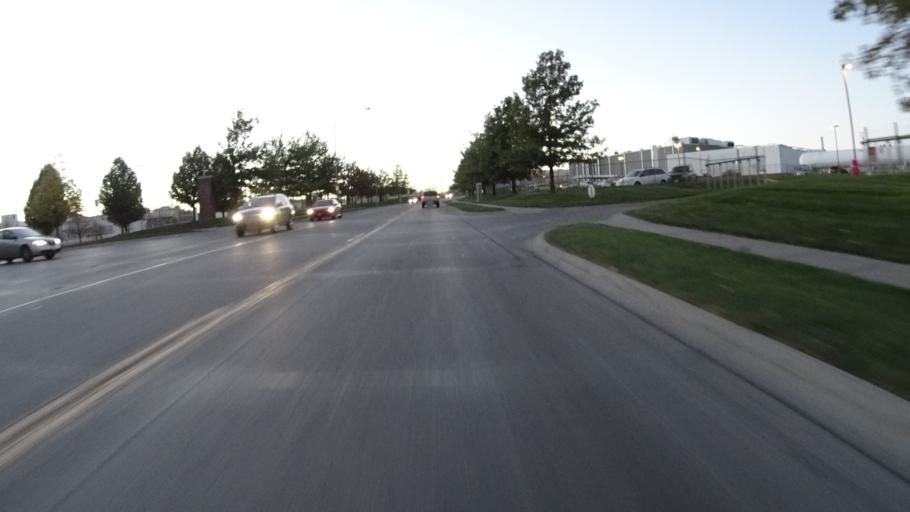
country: US
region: Nebraska
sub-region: Douglas County
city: Omaha
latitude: 41.2092
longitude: -95.9571
